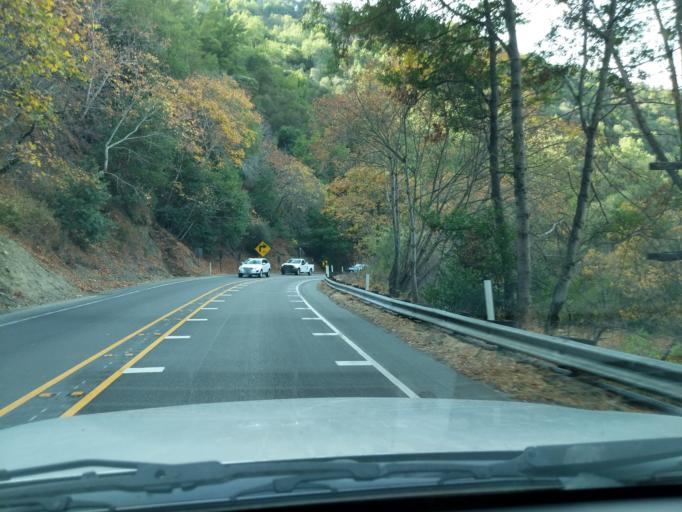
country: US
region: California
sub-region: Alameda County
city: Fremont
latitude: 37.5910
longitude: -121.9354
